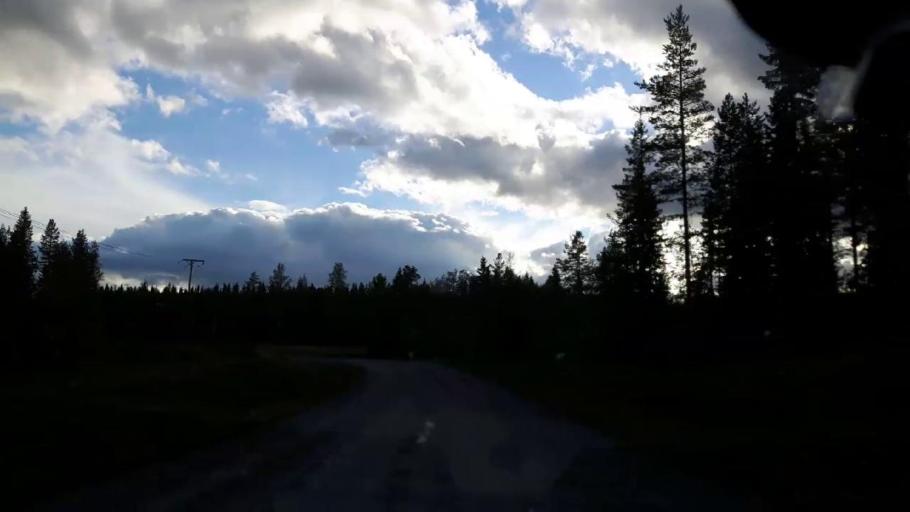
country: SE
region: Jaemtland
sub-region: Stroemsunds Kommun
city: Stroemsund
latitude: 63.3329
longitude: 15.5769
